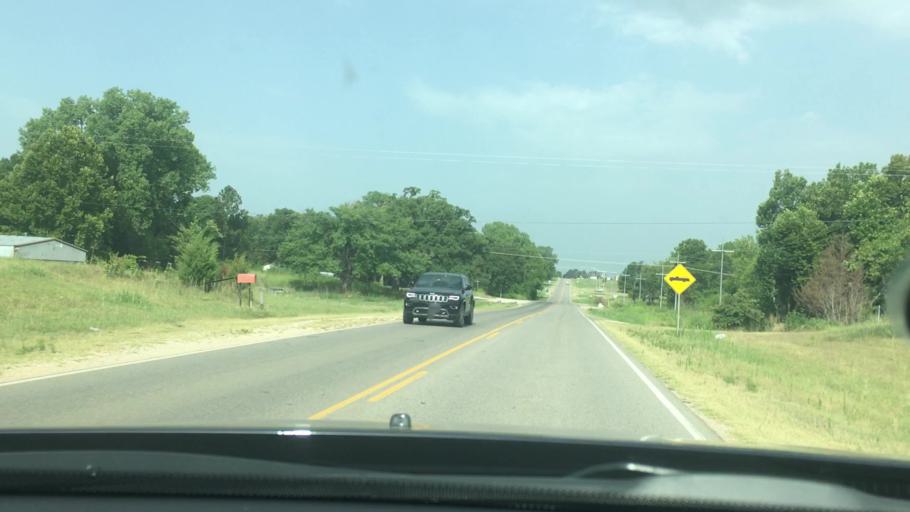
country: US
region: Oklahoma
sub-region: Pontotoc County
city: Ada
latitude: 34.7821
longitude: -96.7728
